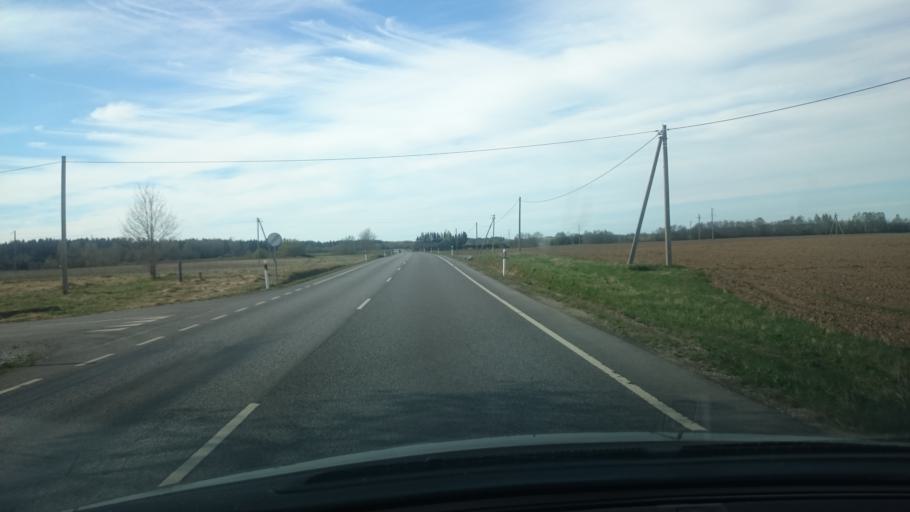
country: EE
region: Ida-Virumaa
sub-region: Johvi vald
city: Johvi
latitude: 59.2760
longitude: 27.5085
